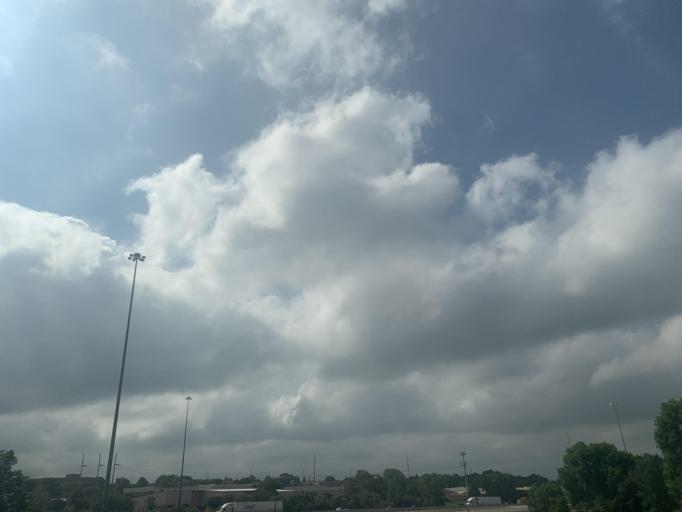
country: US
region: Nebraska
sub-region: Douglas County
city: Ralston
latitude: 41.2105
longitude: -96.0942
